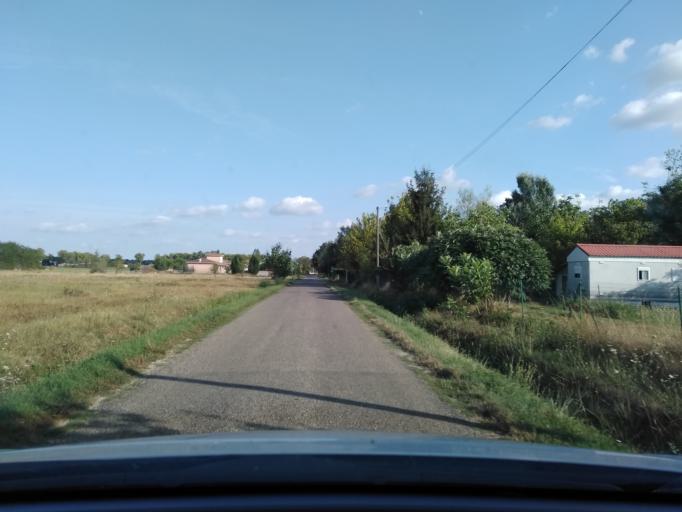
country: FR
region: Midi-Pyrenees
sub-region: Departement du Tarn-et-Garonne
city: Montech
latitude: 43.9686
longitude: 1.2437
